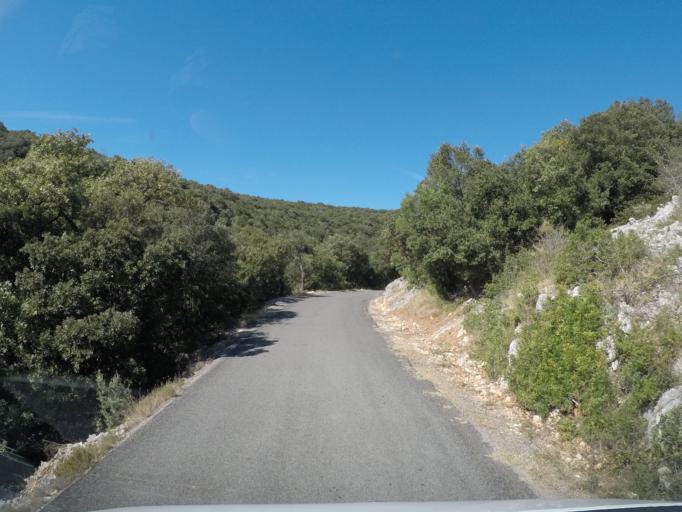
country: FR
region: Languedoc-Roussillon
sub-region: Departement de l'Herault
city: Vailhauques
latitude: 43.7152
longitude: 3.6799
